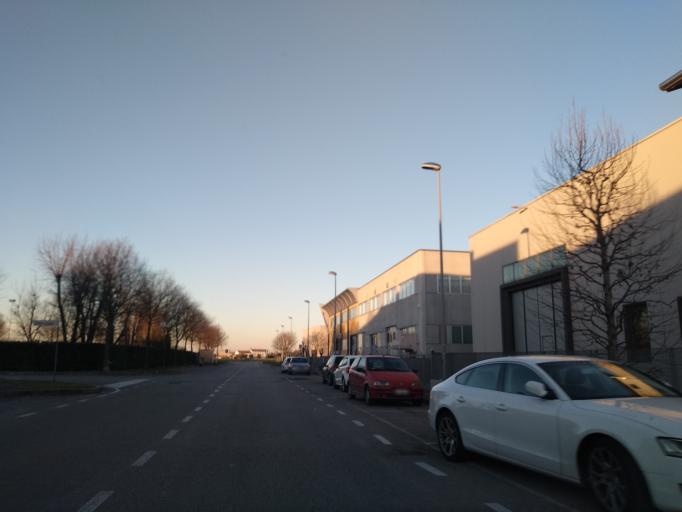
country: IT
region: Veneto
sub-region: Provincia di Padova
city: Mestrino
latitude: 45.4406
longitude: 11.7683
